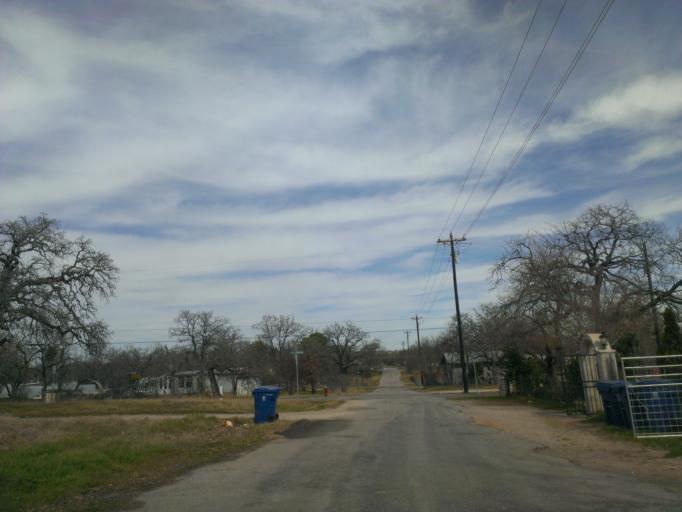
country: US
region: Texas
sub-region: Burnet County
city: Granite Shoals
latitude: 30.5924
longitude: -98.3805
